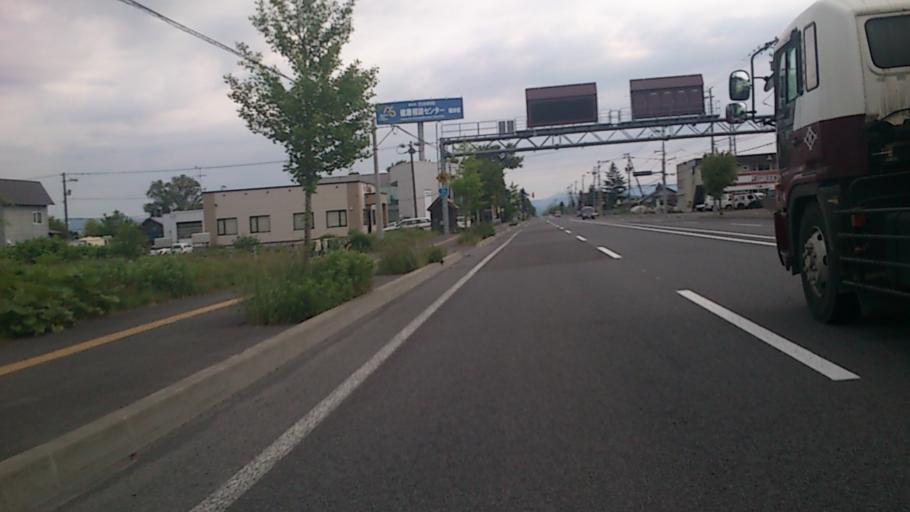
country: JP
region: Hokkaido
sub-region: Asahikawa-shi
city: Asahikawa
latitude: 43.8185
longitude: 142.4465
